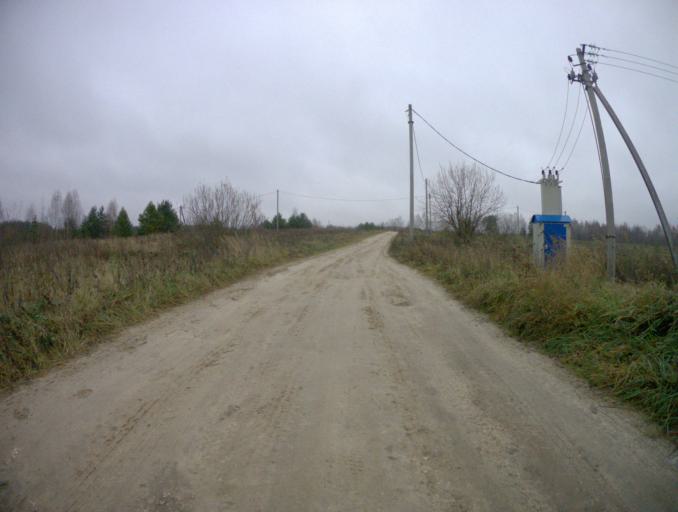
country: RU
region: Vladimir
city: Golovino
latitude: 55.9765
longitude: 40.4580
